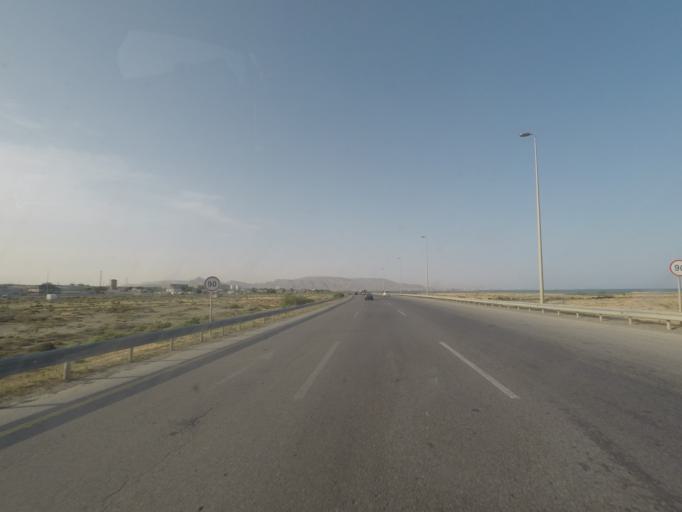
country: AZ
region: Baki
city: Qobustan
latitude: 40.1593
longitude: 49.4628
